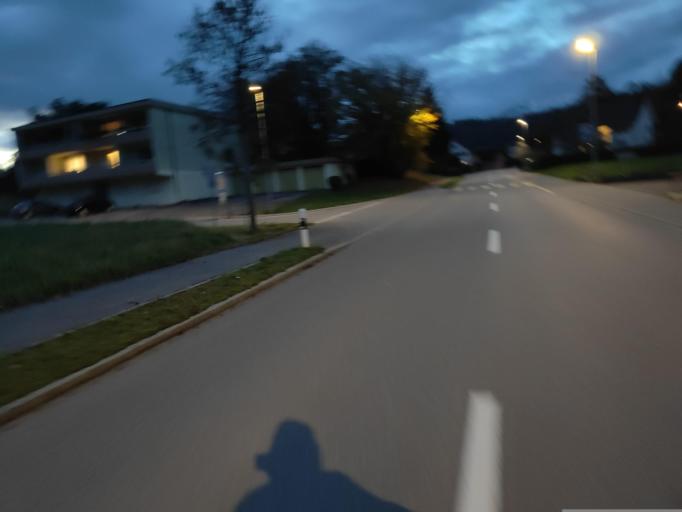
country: LI
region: Mauren
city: Mauren
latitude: 47.2168
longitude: 9.5487
